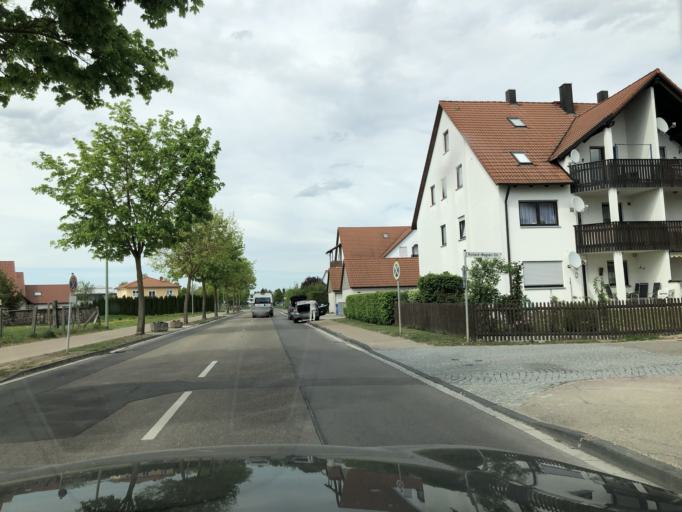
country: DE
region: Bavaria
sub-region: Swabia
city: Mertingen
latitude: 48.6581
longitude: 10.8146
